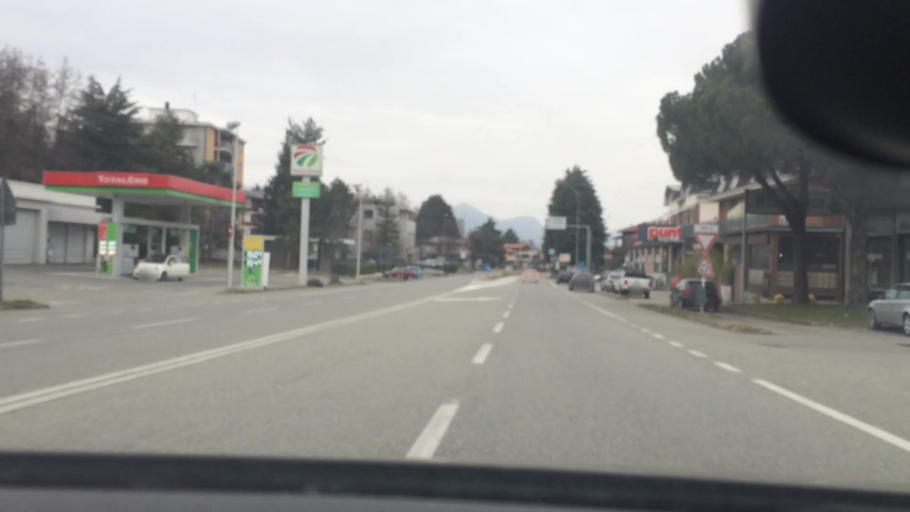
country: IT
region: Lombardy
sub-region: Provincia di Como
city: Lurago d'Erba
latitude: 45.7466
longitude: 9.2198
